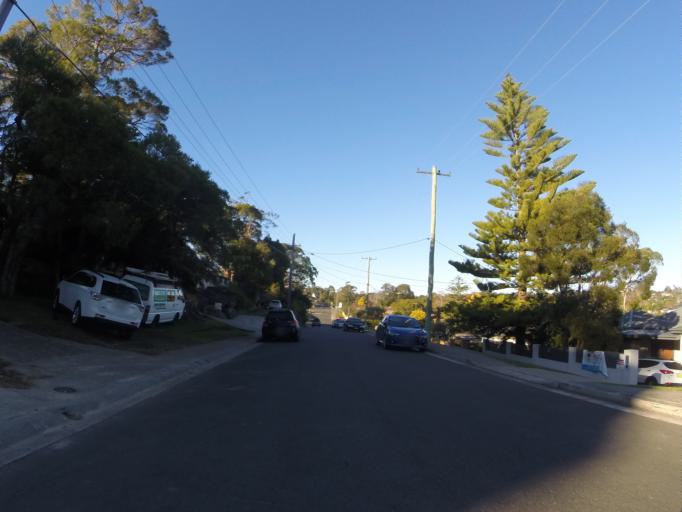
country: AU
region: New South Wales
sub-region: Sutherland Shire
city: Loftus
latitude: -34.0442
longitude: 151.0495
